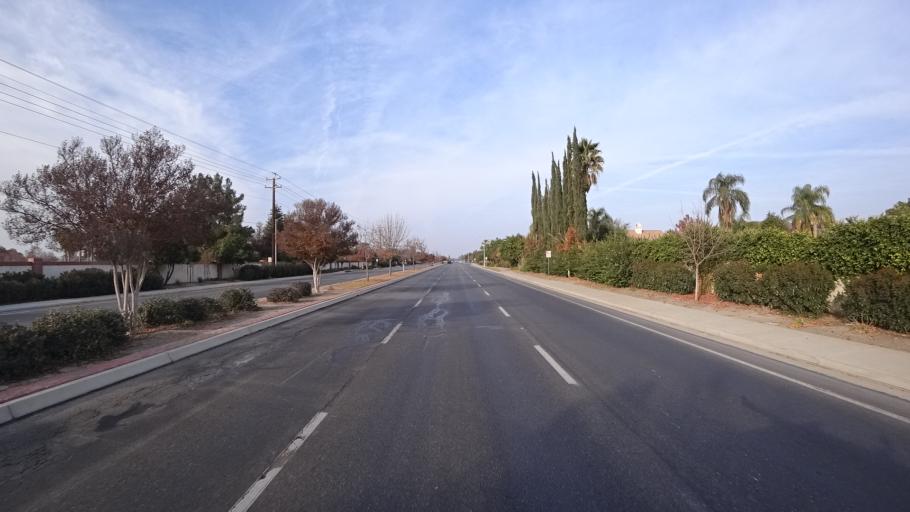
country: US
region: California
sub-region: Kern County
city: Greenacres
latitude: 35.3348
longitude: -119.1279
